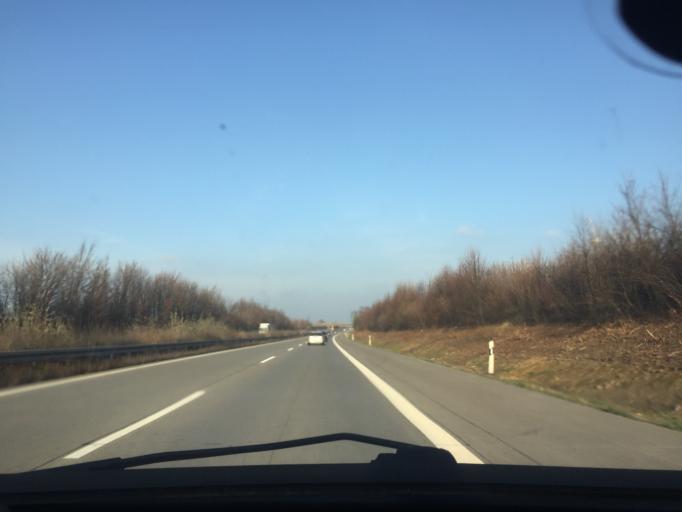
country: DE
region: Saxony-Anhalt
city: Hohendodeleben
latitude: 52.1142
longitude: 11.5281
